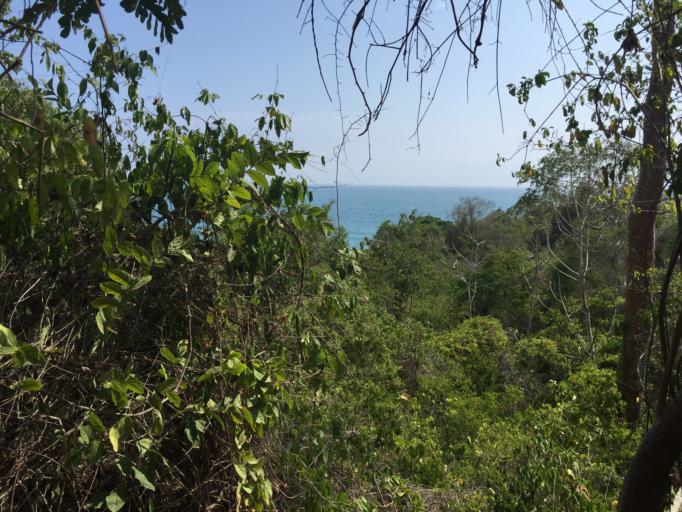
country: CO
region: Magdalena
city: Santa Marta
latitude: 11.3096
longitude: -73.9371
